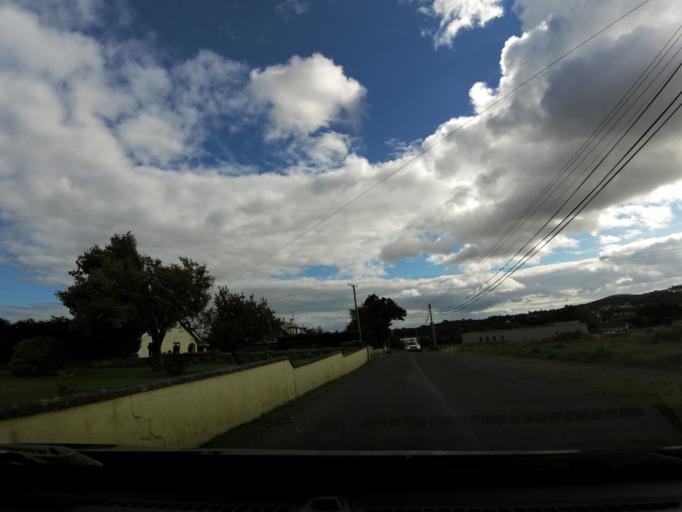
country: IE
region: Connaught
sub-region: County Galway
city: Moycullen
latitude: 53.3476
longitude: -9.1722
